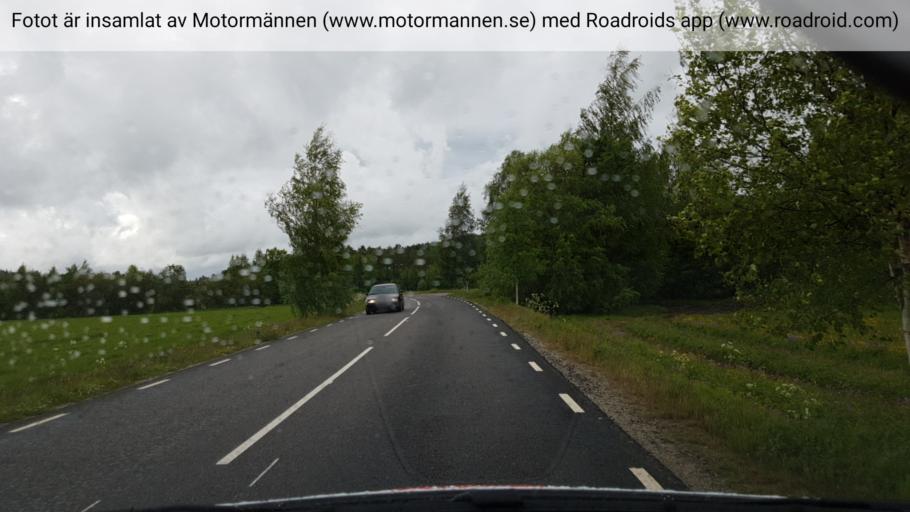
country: SE
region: Vaesterbotten
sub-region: Vannas Kommun
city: Vannasby
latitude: 63.8855
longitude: 19.8882
